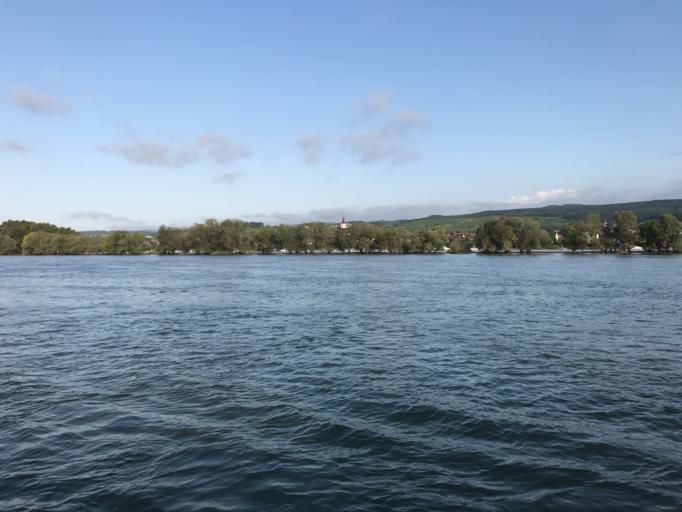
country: DE
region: Rheinland-Pfalz
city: Oestrich-Winkel
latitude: 49.9959
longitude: 8.0199
